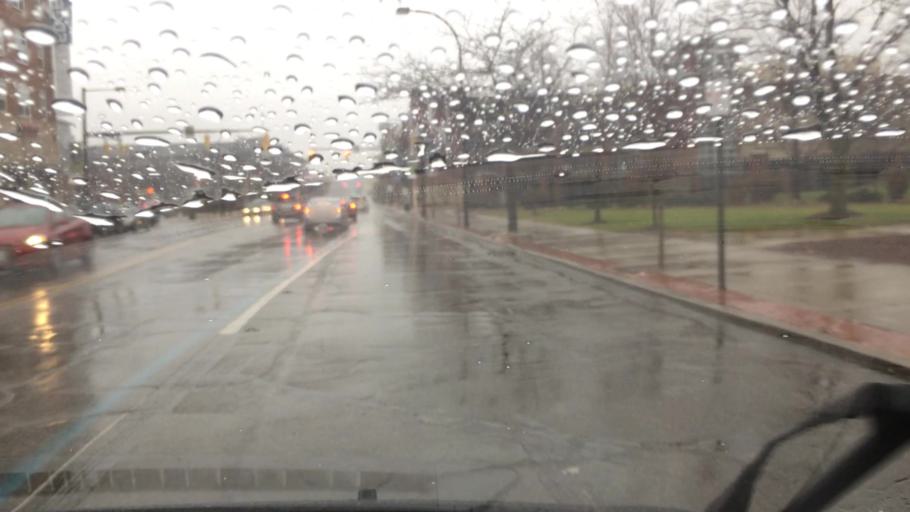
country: US
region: Ohio
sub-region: Summit County
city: Akron
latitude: 41.0729
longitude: -81.5127
